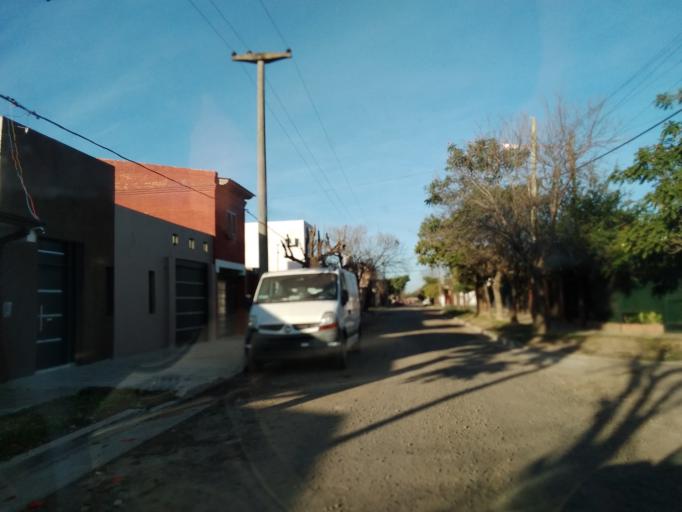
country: AR
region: Corrientes
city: Corrientes
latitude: -27.5006
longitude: -58.8341
